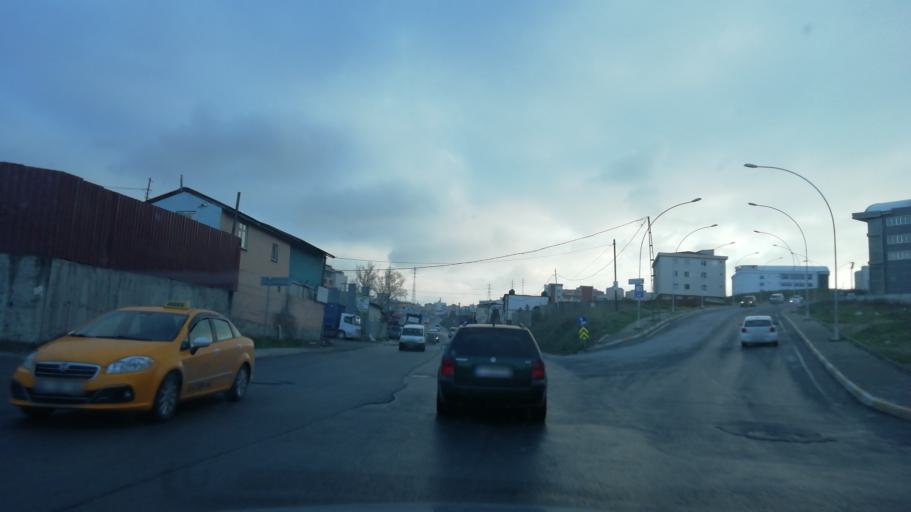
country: TR
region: Istanbul
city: Esenyurt
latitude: 41.0275
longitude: 28.7017
